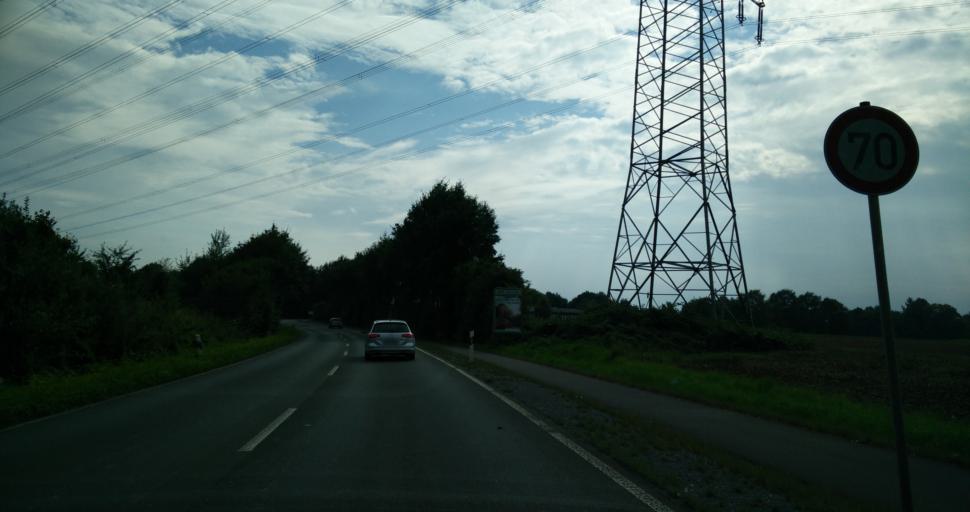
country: DE
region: North Rhine-Westphalia
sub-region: Regierungsbezirk Dusseldorf
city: Mettmann
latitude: 51.2399
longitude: 7.0054
